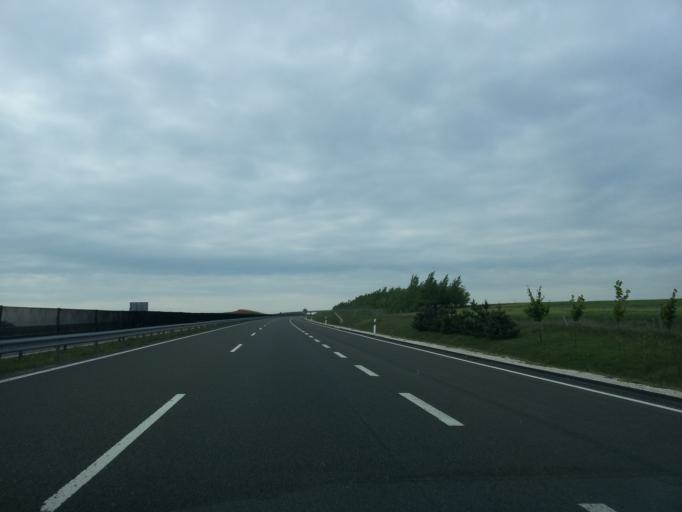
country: HU
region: Tolna
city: Dunafoldvar
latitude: 46.7702
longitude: 18.8722
